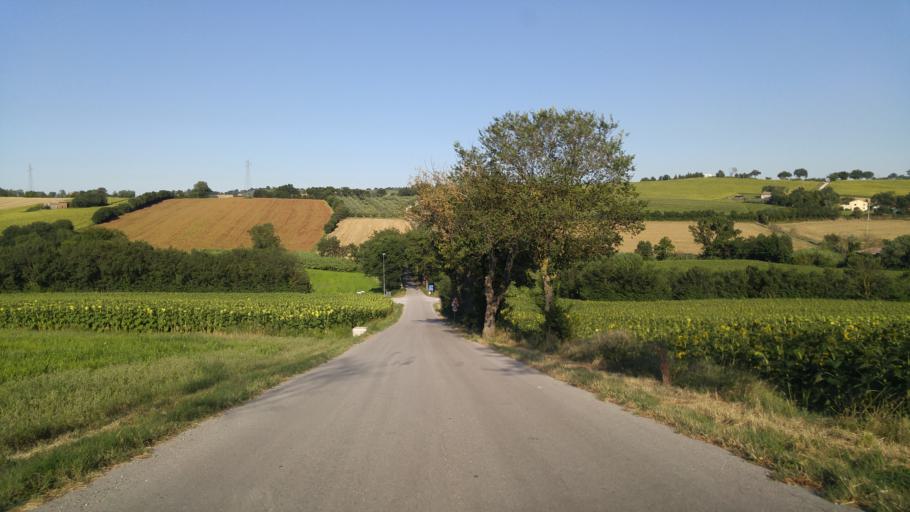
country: IT
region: The Marches
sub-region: Provincia di Pesaro e Urbino
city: Mombaroccio
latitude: 43.8115
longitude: 12.8787
